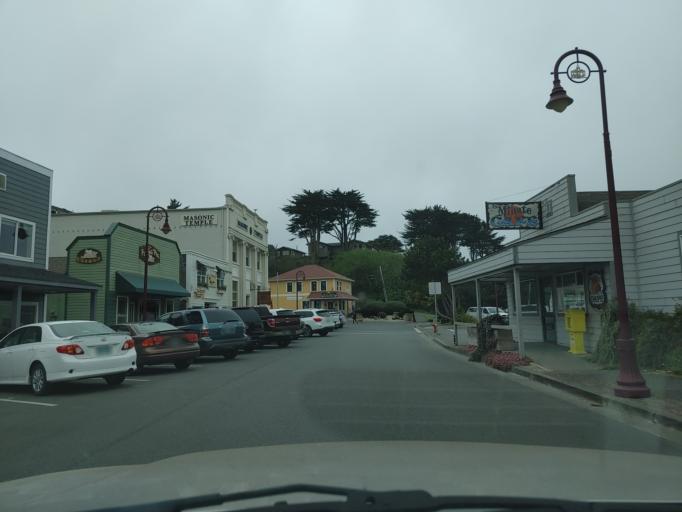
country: US
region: Oregon
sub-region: Coos County
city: Bandon
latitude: 43.1191
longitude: -124.4139
